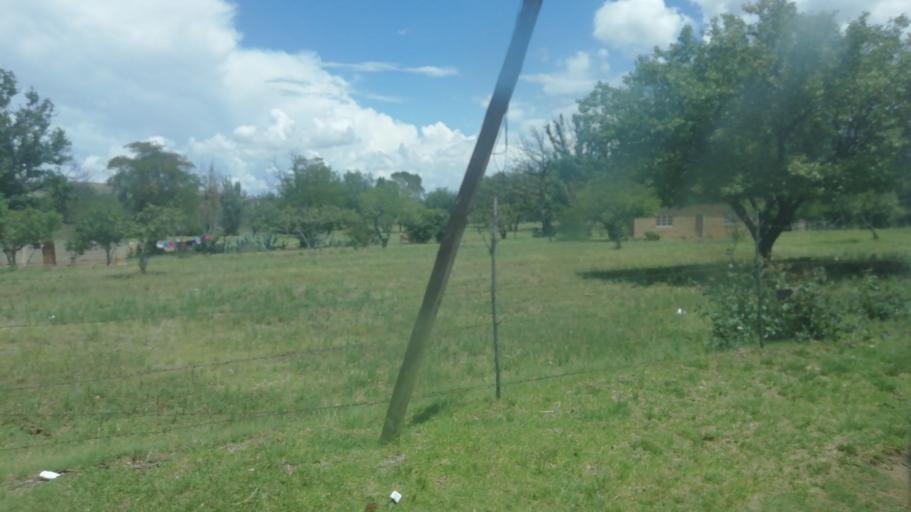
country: LS
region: Maseru
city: Nako
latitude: -29.6199
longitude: 27.5100
